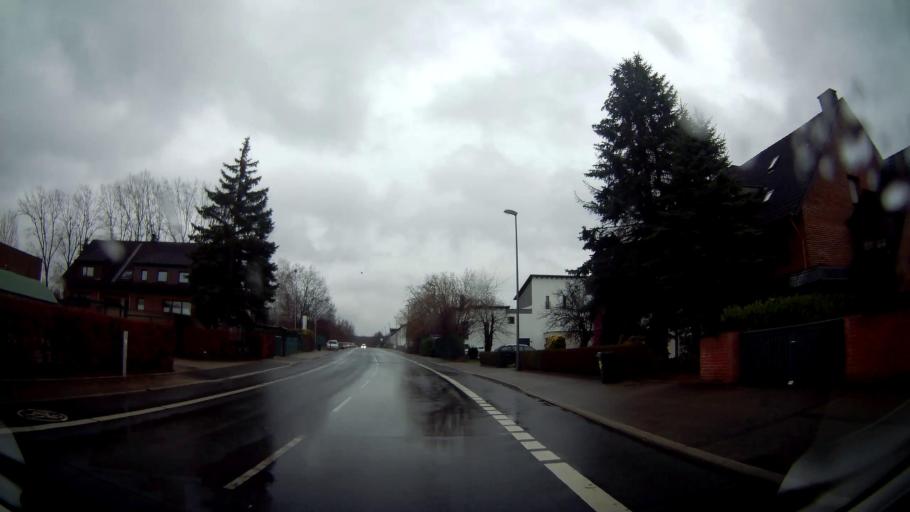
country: DE
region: North Rhine-Westphalia
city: Bochum-Hordel
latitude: 51.5201
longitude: 7.1981
